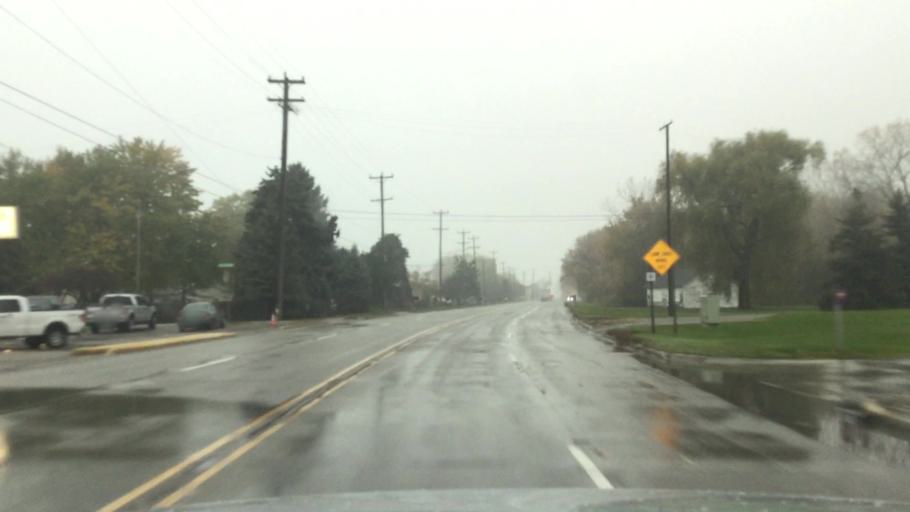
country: US
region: Michigan
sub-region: Macomb County
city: New Baltimore
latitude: 42.6811
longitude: -82.6607
